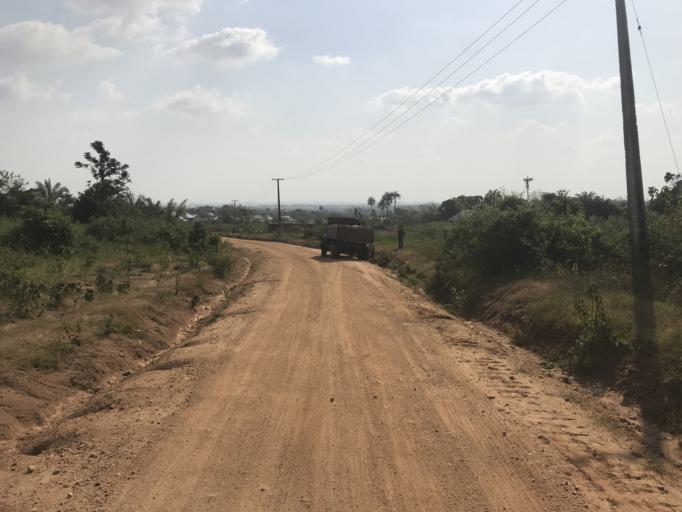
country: NG
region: Osun
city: Osogbo
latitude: 7.8473
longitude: 4.5817
